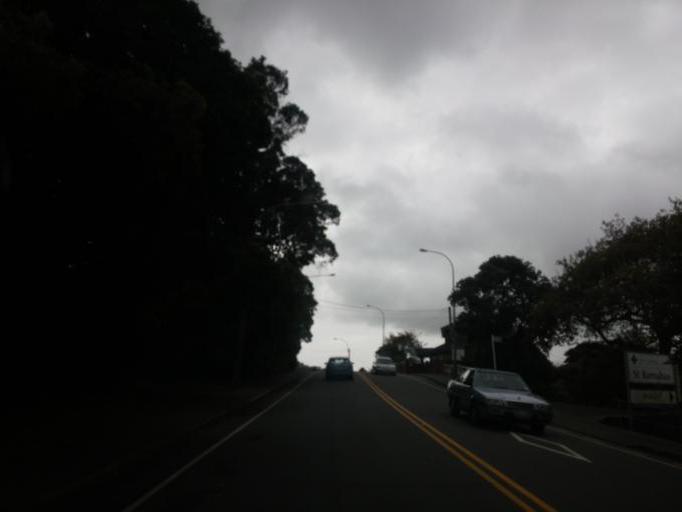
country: NZ
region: Wellington
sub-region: Wellington City
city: Wellington
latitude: -41.2445
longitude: 174.7908
